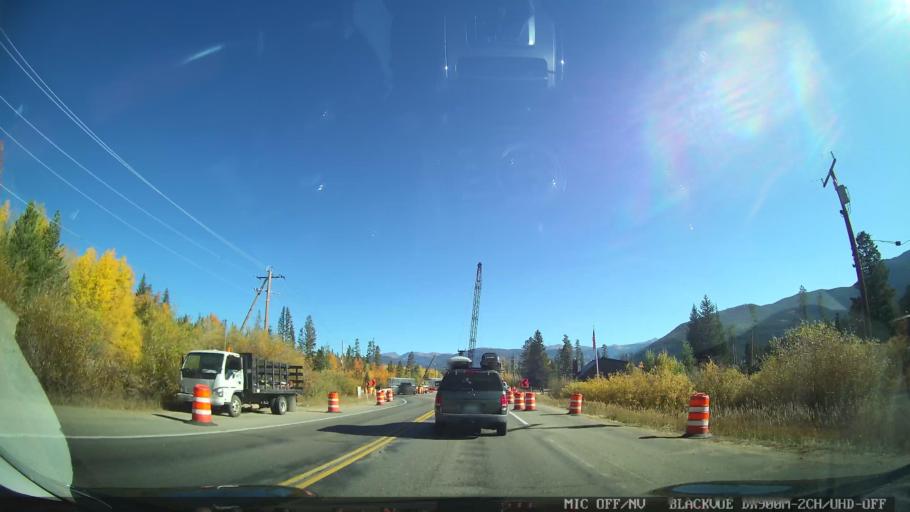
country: US
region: Colorado
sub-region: Grand County
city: Granby
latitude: 40.2184
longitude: -105.8595
